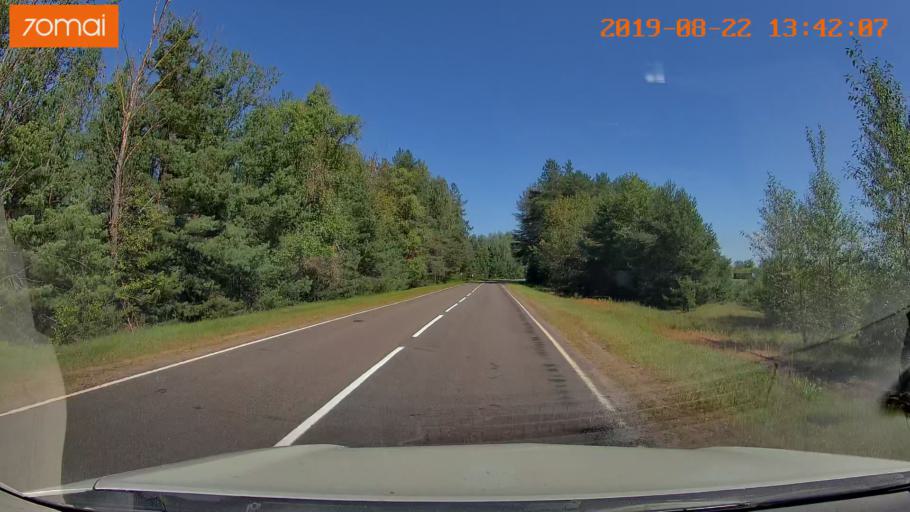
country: BY
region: Mogilev
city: Asipovichy
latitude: 53.2403
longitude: 28.4102
